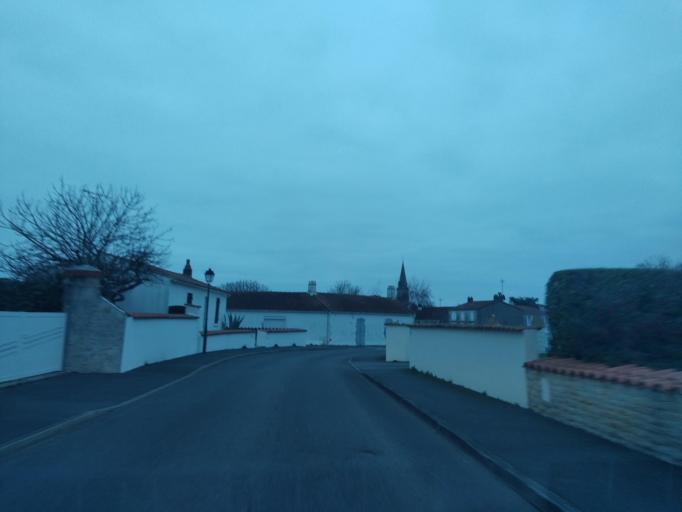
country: FR
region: Pays de la Loire
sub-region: Departement de la Vendee
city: Triaize
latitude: 46.3535
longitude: -1.2542
